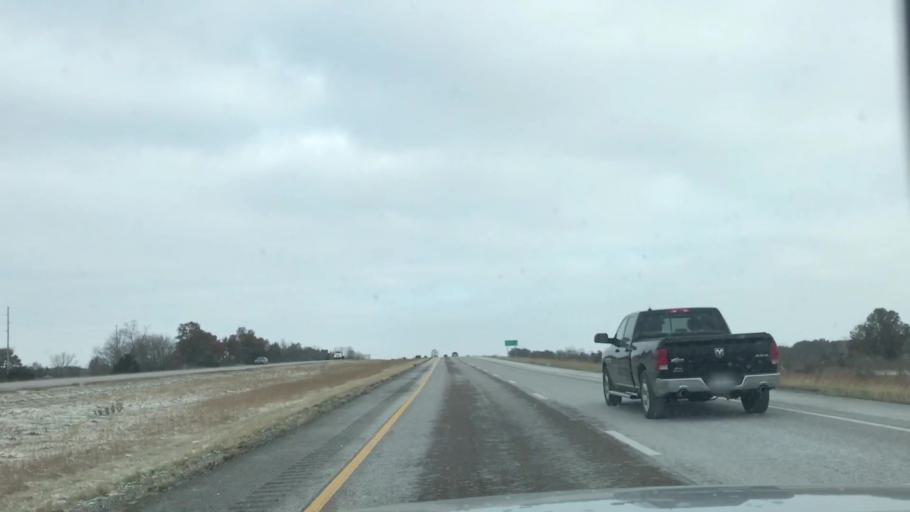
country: US
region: Illinois
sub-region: Macoupin County
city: Staunton
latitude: 38.9748
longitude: -89.7492
